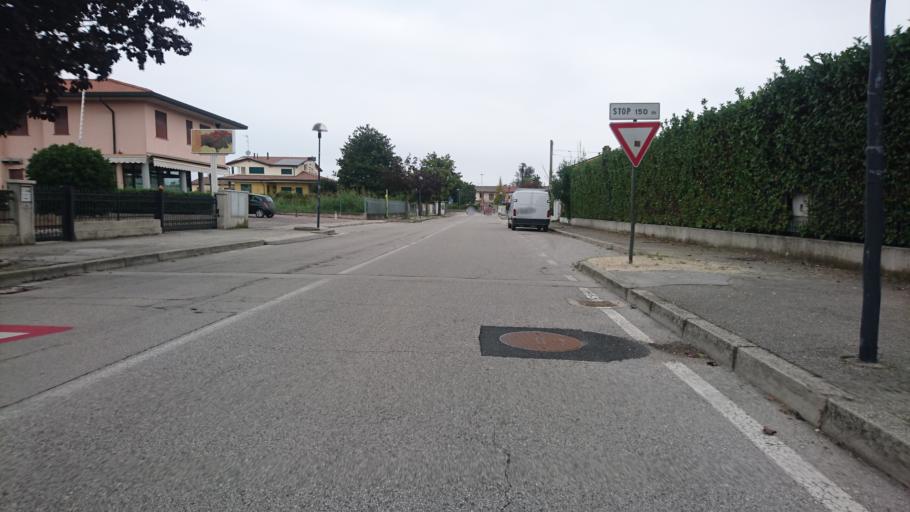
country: IT
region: Veneto
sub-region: Provincia di Padova
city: Santa Maria di Non
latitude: 45.5134
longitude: 11.8518
